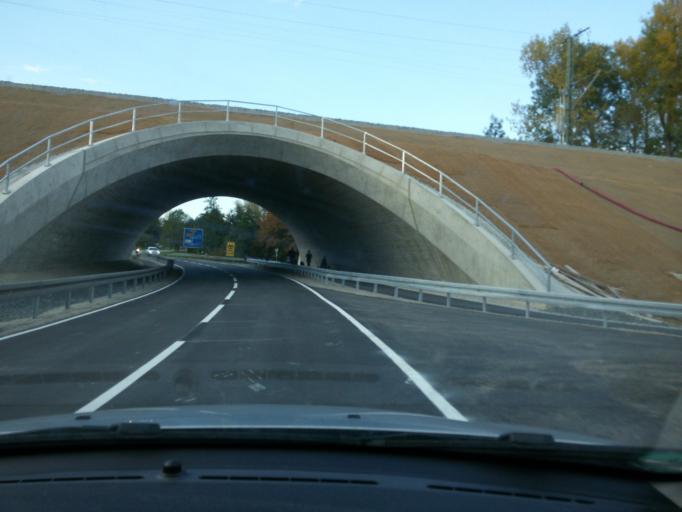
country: DE
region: Bavaria
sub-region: Swabia
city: Stetten
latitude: 48.0289
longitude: 10.4423
